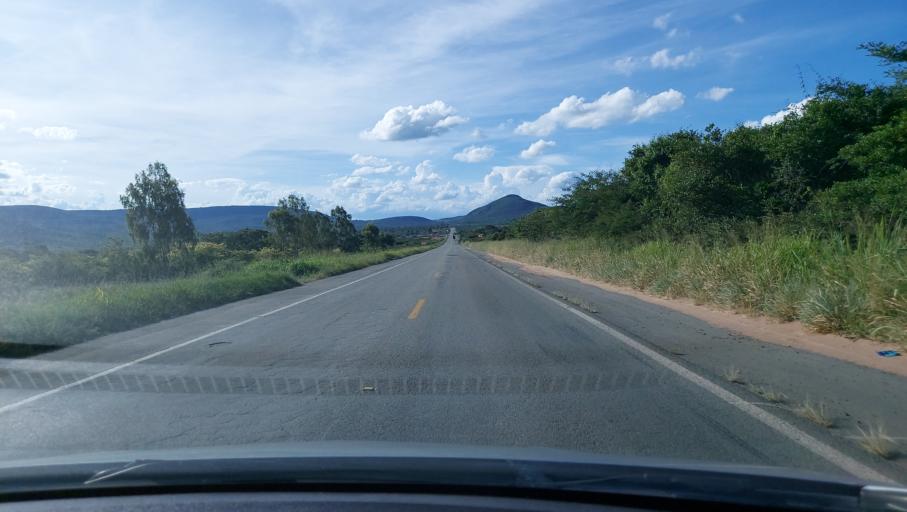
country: BR
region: Bahia
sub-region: Seabra
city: Seabra
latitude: -12.4257
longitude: -41.8330
